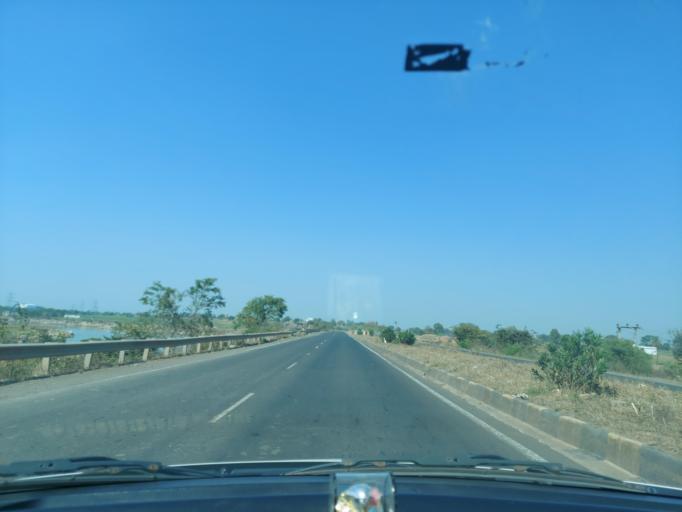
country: IN
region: Madhya Pradesh
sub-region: Indore
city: Manpur
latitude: 22.4876
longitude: 75.5676
